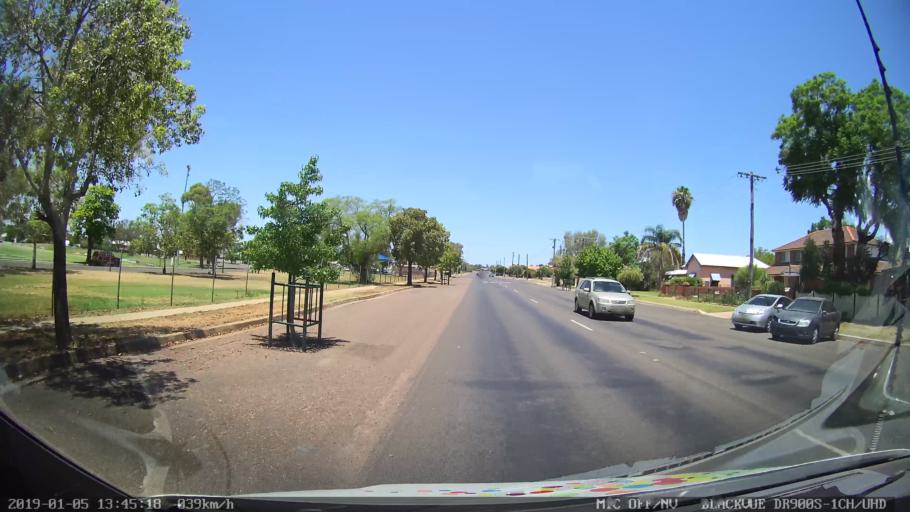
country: AU
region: New South Wales
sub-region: Gunnedah
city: Gunnedah
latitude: -30.9825
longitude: 150.2609
